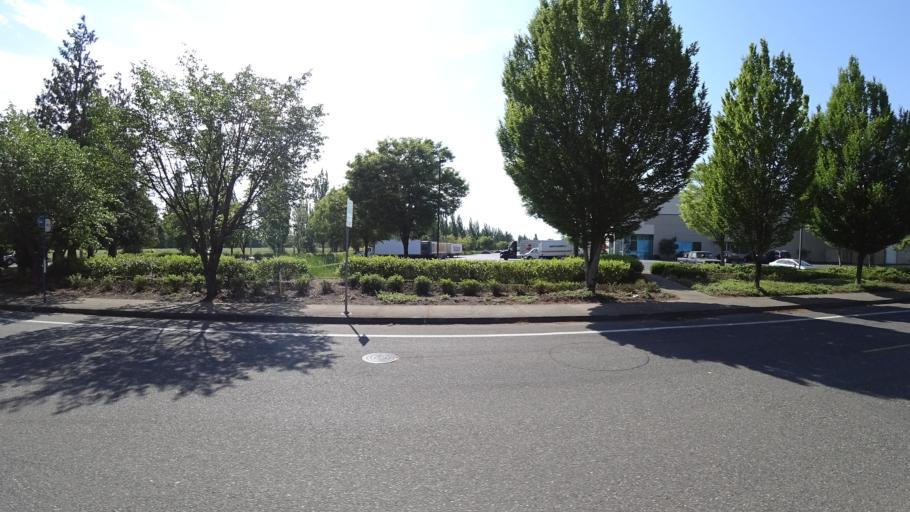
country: US
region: Oregon
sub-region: Multnomah County
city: Fairview
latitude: 45.5580
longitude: -122.5002
